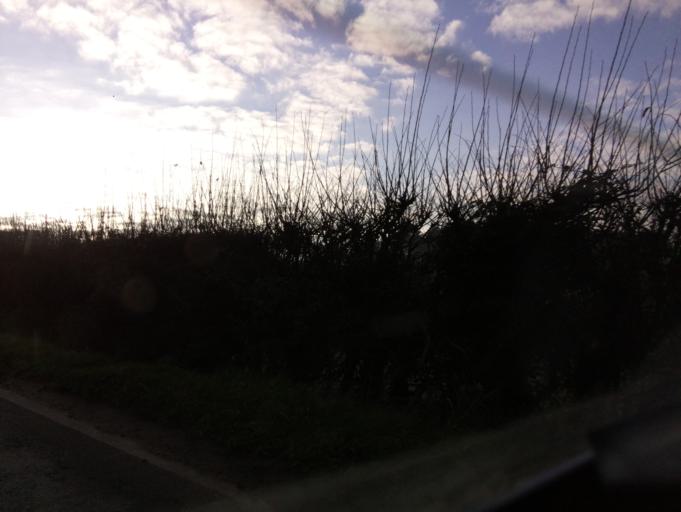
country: GB
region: England
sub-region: Warwickshire
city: Curdworth
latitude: 52.5657
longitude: -1.7597
